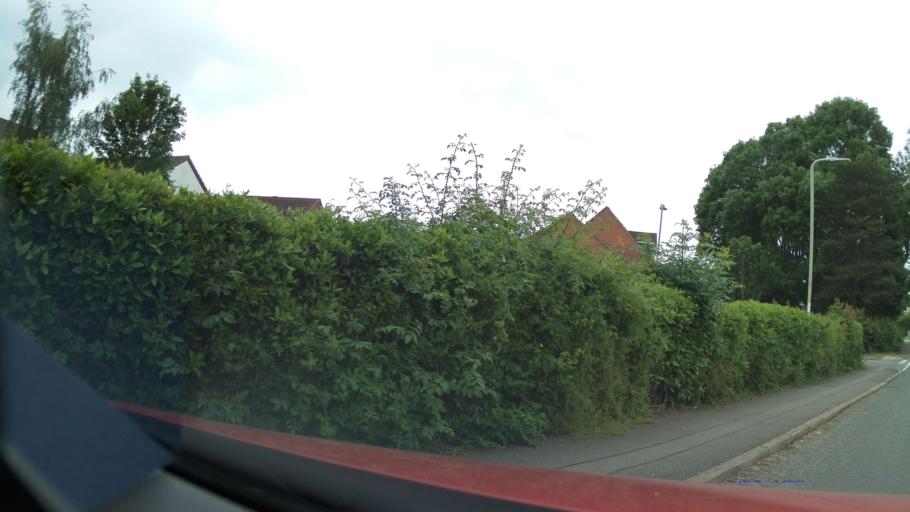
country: GB
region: England
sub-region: District of Rutland
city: Oakham
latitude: 52.6711
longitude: -0.7454
